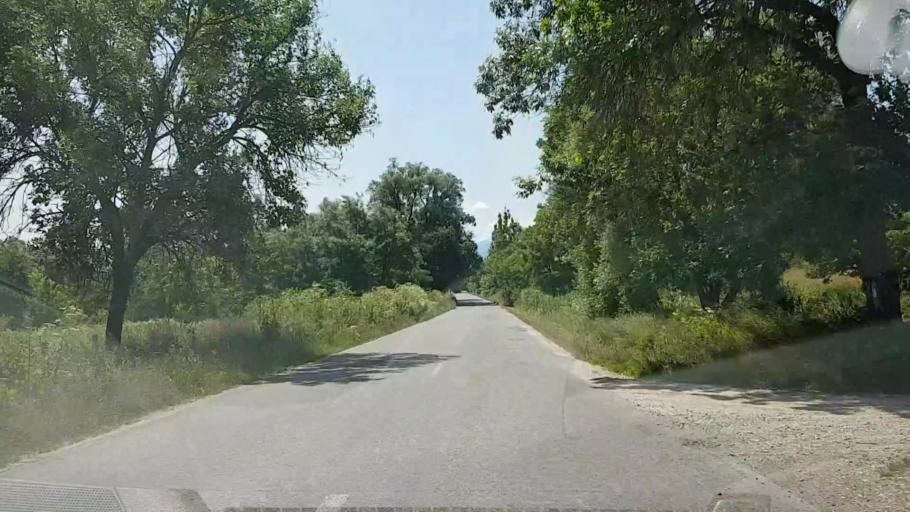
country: RO
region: Brasov
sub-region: Comuna Voila
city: Voila
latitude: 45.8497
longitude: 24.8323
